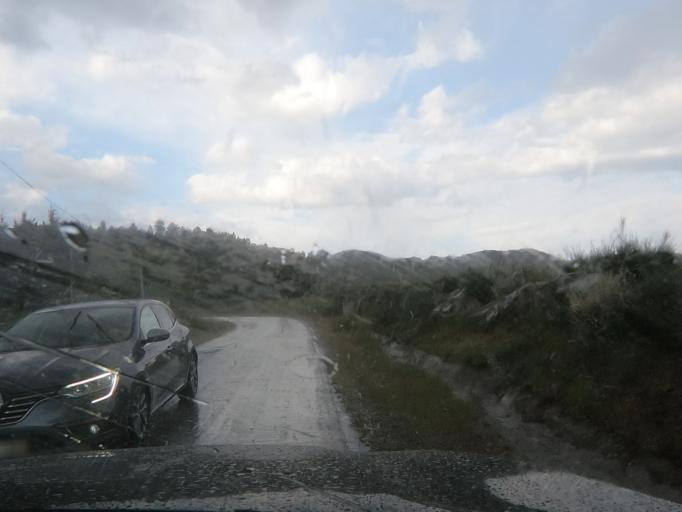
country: PT
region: Vila Real
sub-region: Vila Real
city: Vila Real
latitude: 41.3649
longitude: -7.6971
